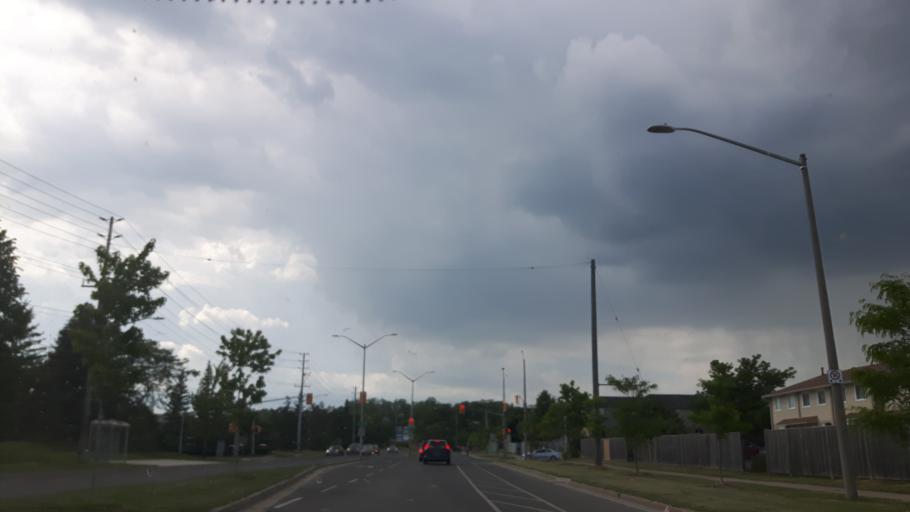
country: CA
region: Ontario
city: London
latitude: 42.9416
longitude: -81.2126
